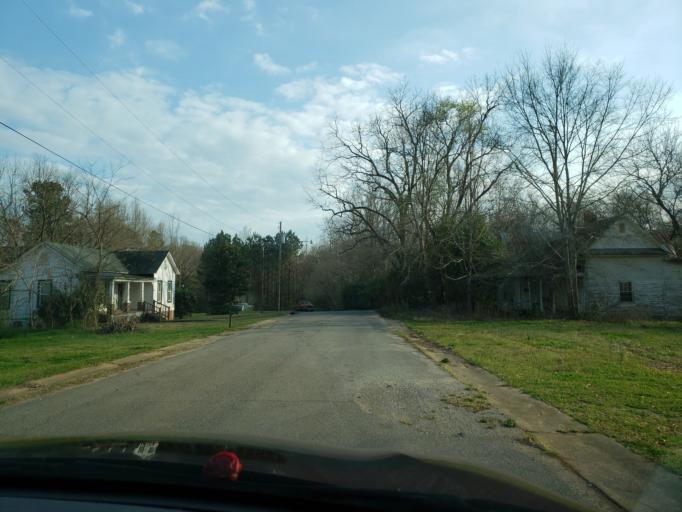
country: US
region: Alabama
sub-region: Hale County
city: Greensboro
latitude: 32.6992
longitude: -87.6054
